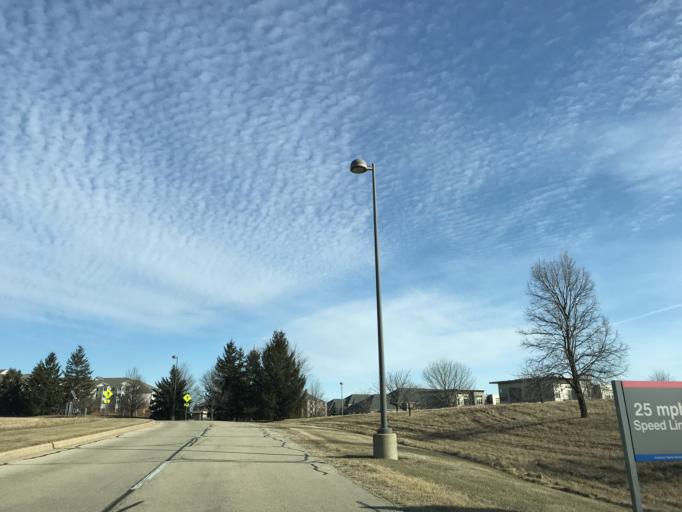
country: US
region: Wisconsin
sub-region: Dane County
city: Sun Prairie
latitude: 43.1540
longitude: -89.2871
